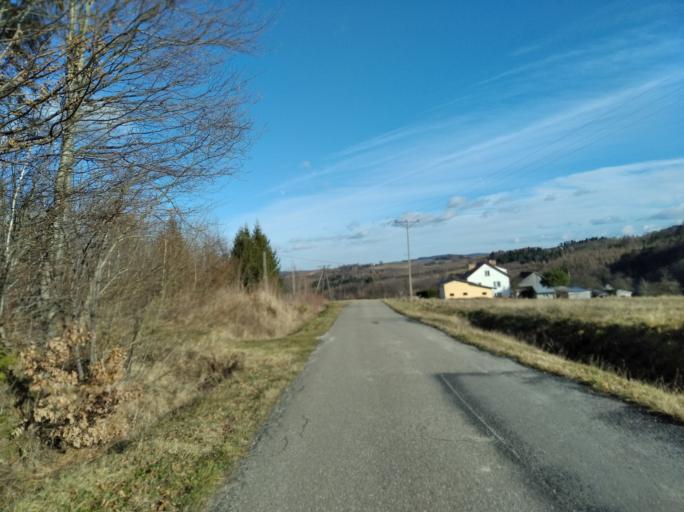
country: PL
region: Subcarpathian Voivodeship
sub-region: Powiat strzyzowski
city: Wisniowa
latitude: 49.8998
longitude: 21.6764
